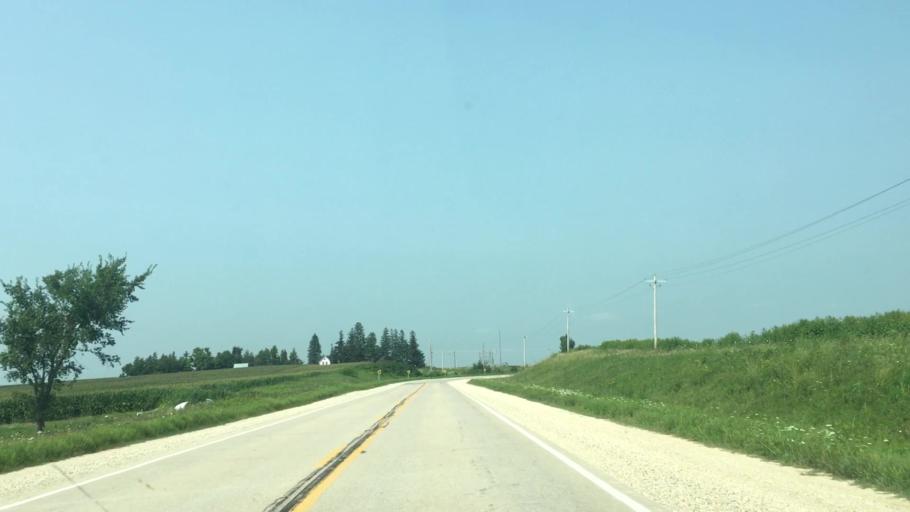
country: US
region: Iowa
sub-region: Fayette County
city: West Union
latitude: 43.1357
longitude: -91.8691
